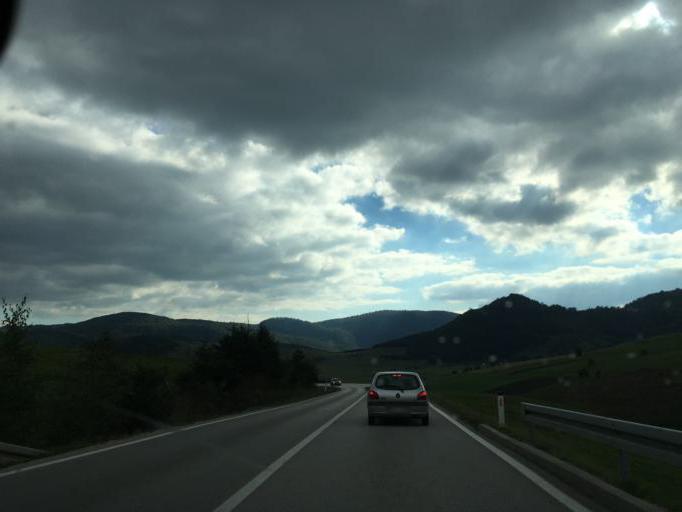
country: BA
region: Federation of Bosnia and Herzegovina
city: Novi Travnik
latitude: 44.1133
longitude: 17.5758
